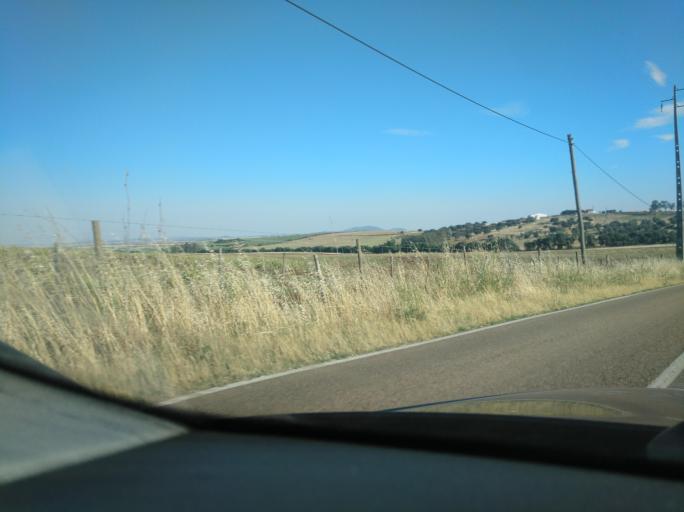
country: PT
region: Portalegre
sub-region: Elvas
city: Elvas
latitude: 38.8294
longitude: -7.1653
